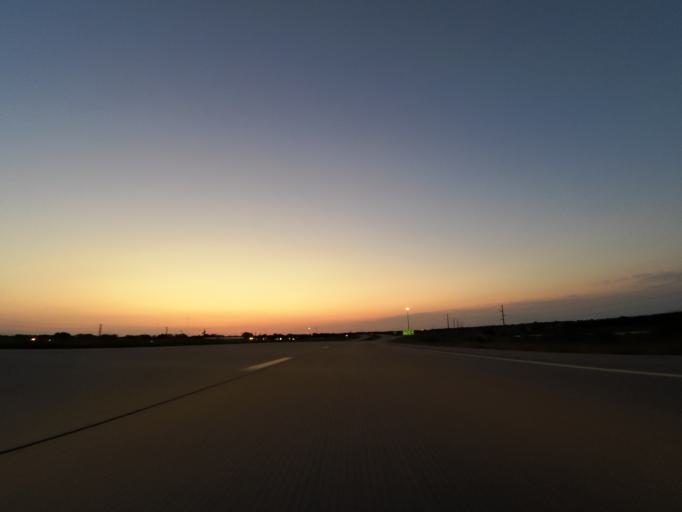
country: US
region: Kansas
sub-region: Reno County
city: South Hutchinson
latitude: 38.0130
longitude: -97.9293
